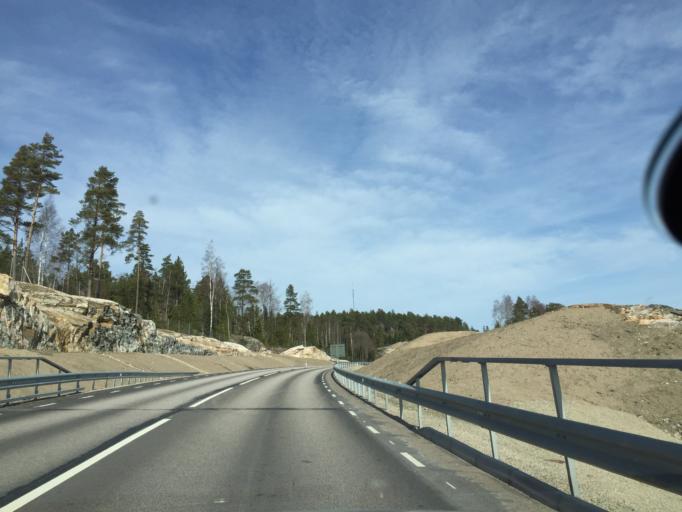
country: SE
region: Vaestra Goetaland
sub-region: Uddevalla Kommun
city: Uddevalla
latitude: 58.3526
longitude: 11.8024
